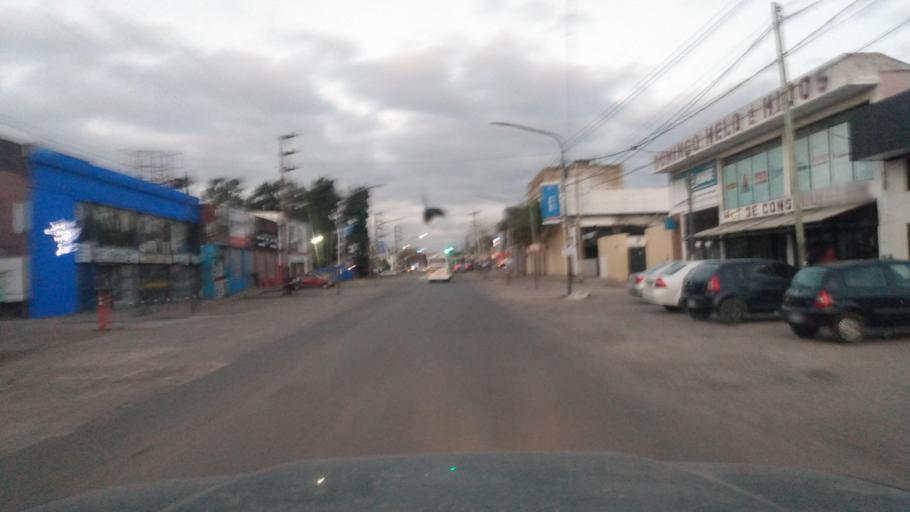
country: AR
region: Buenos Aires
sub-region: Partido de Pilar
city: Pilar
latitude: -34.4544
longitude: -58.9115
